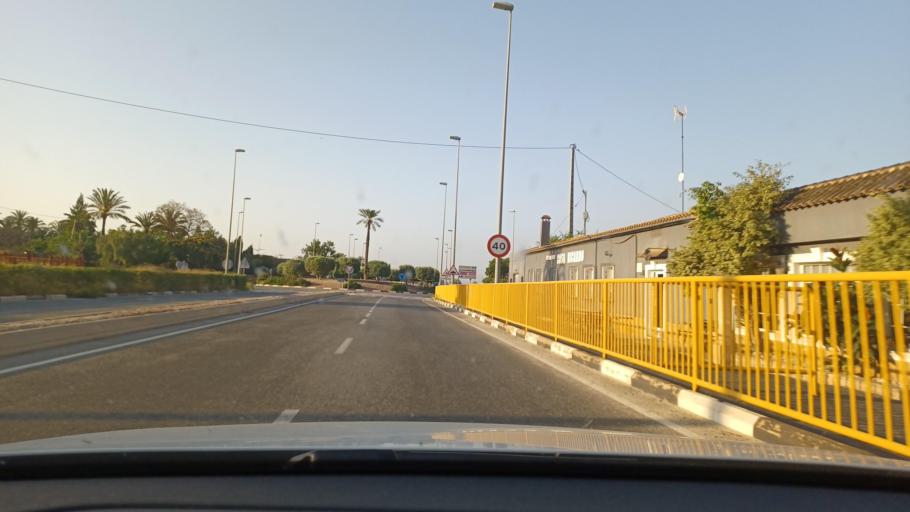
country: ES
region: Valencia
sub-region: Provincia de Alicante
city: Elche
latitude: 38.2409
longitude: -0.7005
